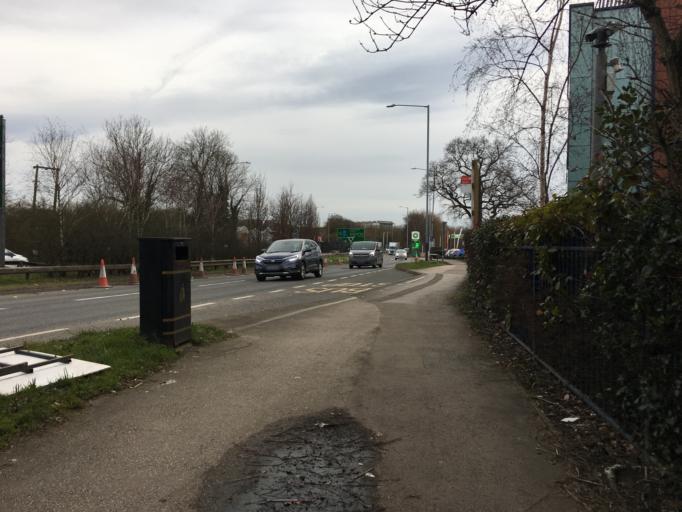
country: GB
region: England
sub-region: Warwickshire
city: Rugby
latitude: 52.3850
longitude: -1.2647
